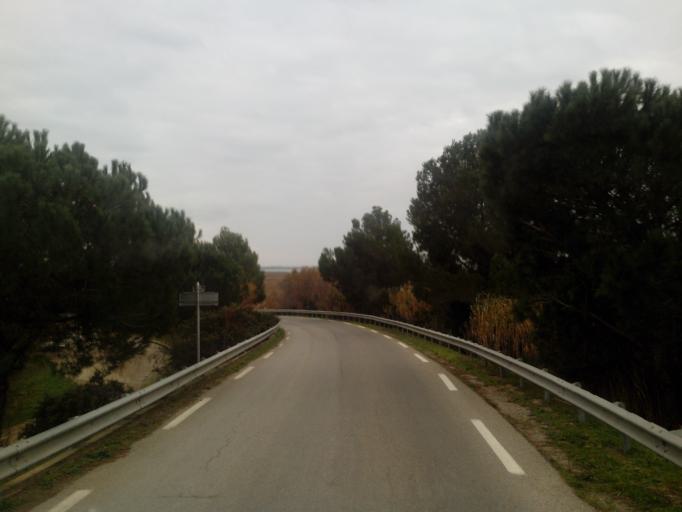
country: FR
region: Languedoc-Roussillon
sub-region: Departement du Gard
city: Vauvert
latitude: 43.6376
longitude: 4.2985
